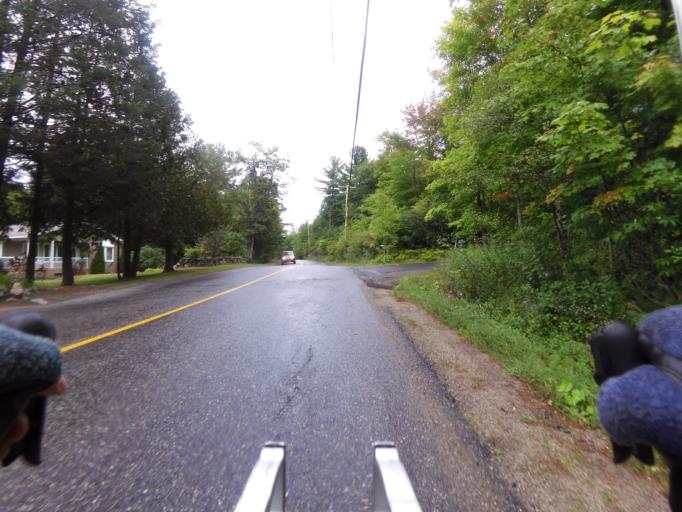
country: CA
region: Quebec
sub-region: Outaouais
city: Gatineau
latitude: 45.5398
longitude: -75.7446
